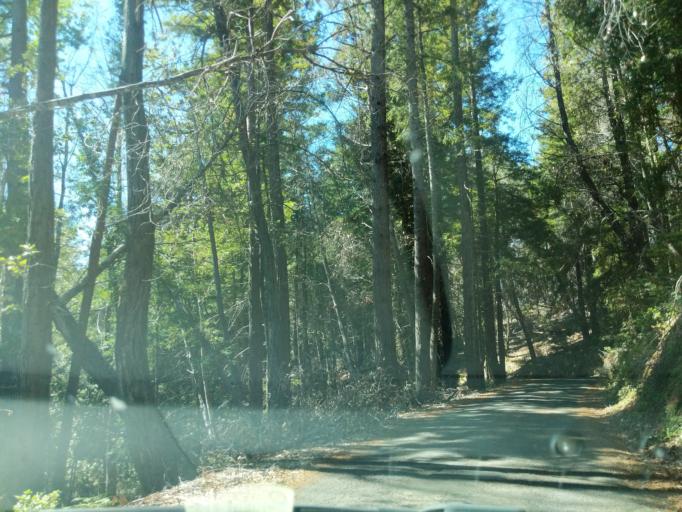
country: US
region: California
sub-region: Sonoma County
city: Monte Rio
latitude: 38.5258
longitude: -123.2278
